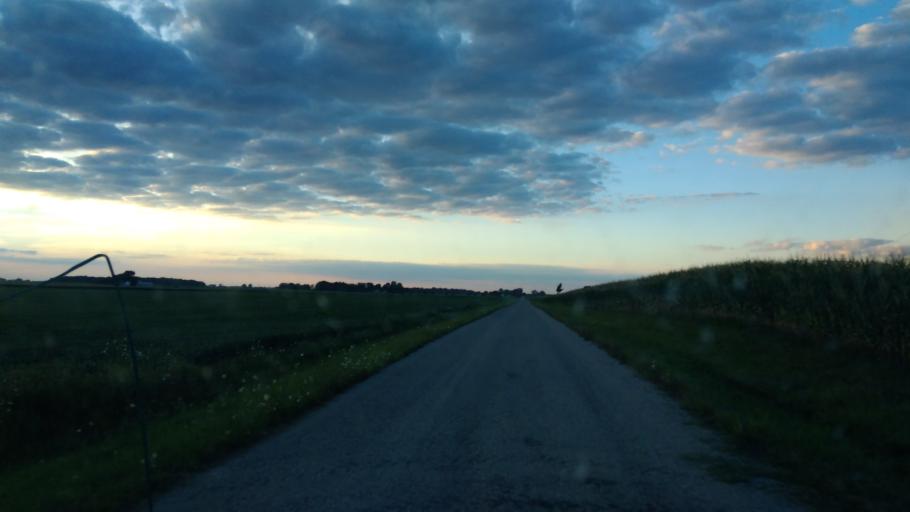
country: US
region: Indiana
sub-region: Adams County
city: Geneva
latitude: 40.6159
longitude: -85.0600
